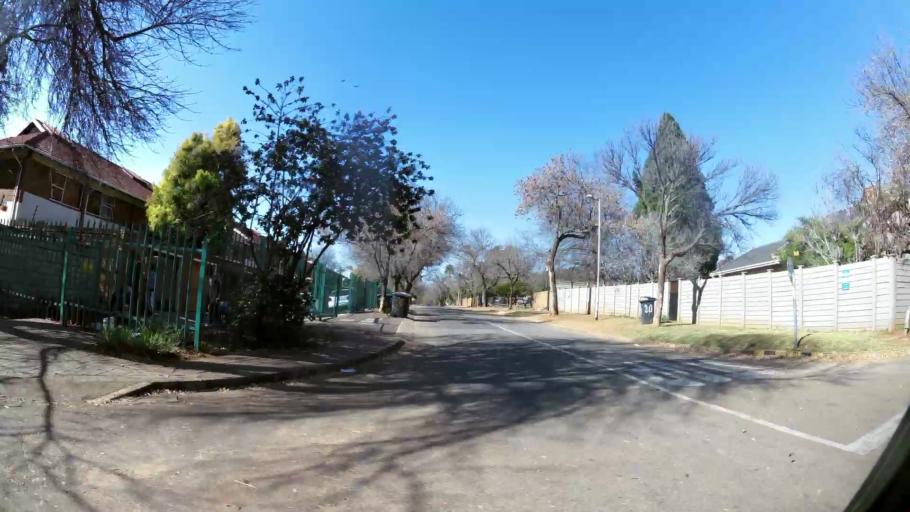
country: ZA
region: Gauteng
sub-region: City of Johannesburg Metropolitan Municipality
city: Roodepoort
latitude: -26.1251
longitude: 27.9689
